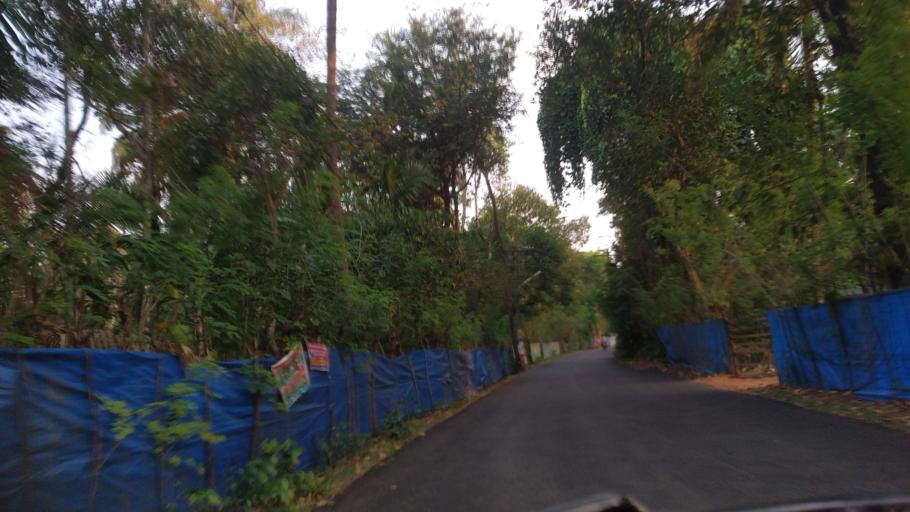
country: IN
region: Kerala
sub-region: Thrissur District
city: Thanniyam
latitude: 10.3554
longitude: 76.1119
